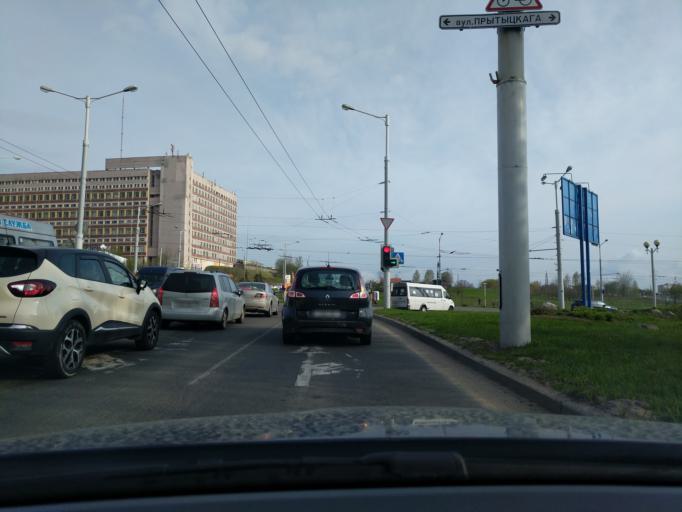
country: BY
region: Minsk
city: Novoye Medvezhino
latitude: 53.9064
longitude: 27.4625
